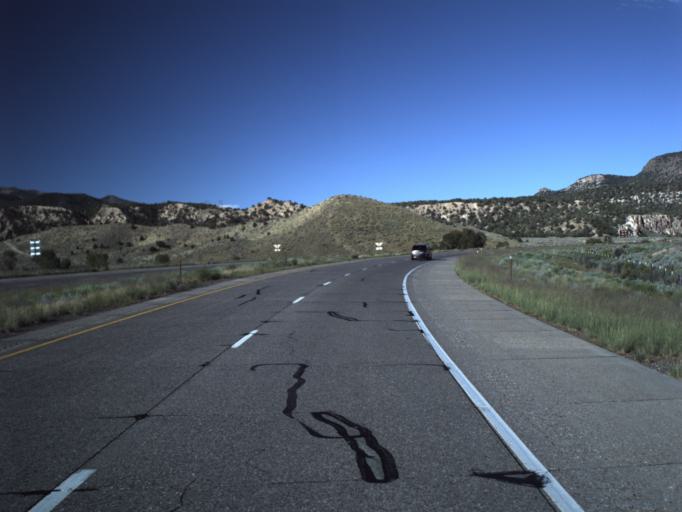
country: US
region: Utah
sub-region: Sevier County
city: Monroe
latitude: 38.5771
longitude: -112.3318
